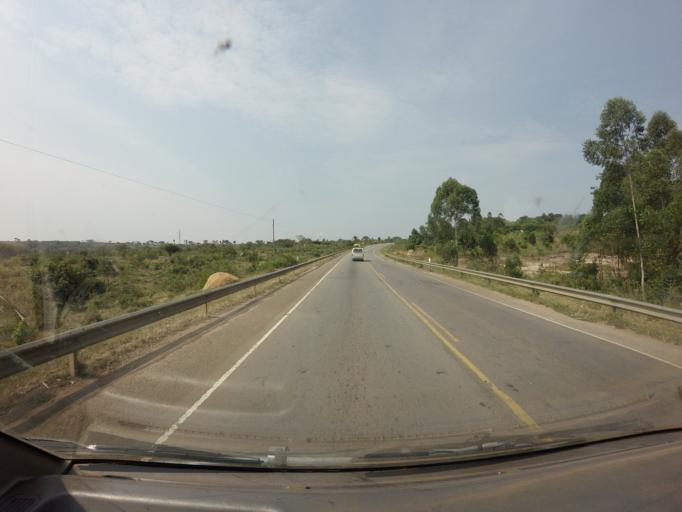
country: UG
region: Central Region
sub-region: Lwengo District
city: Lwengo
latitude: -0.3988
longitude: 31.3973
